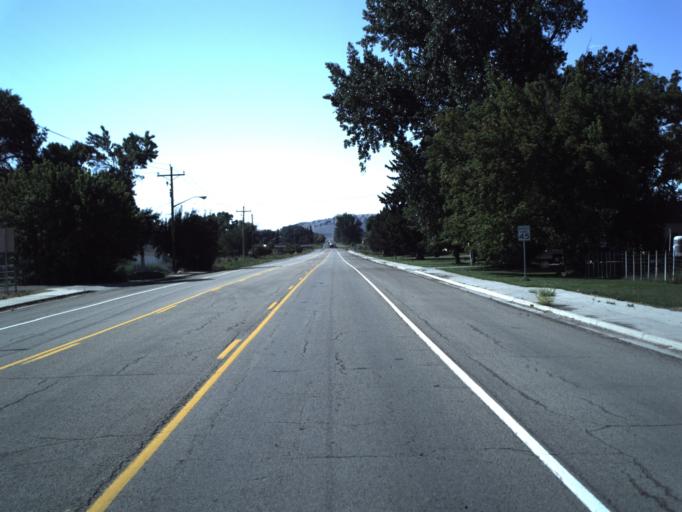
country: US
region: Utah
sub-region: Emery County
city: Ferron
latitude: 39.0854
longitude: -111.1320
